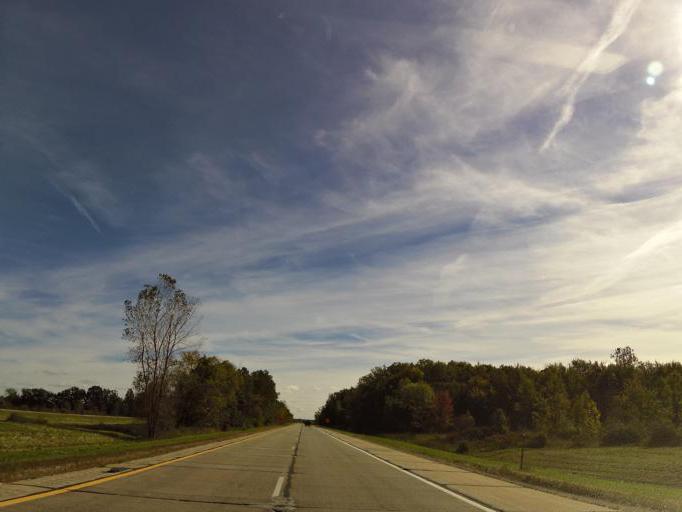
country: US
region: Michigan
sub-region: Macomb County
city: Memphis
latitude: 42.9770
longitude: -82.8181
